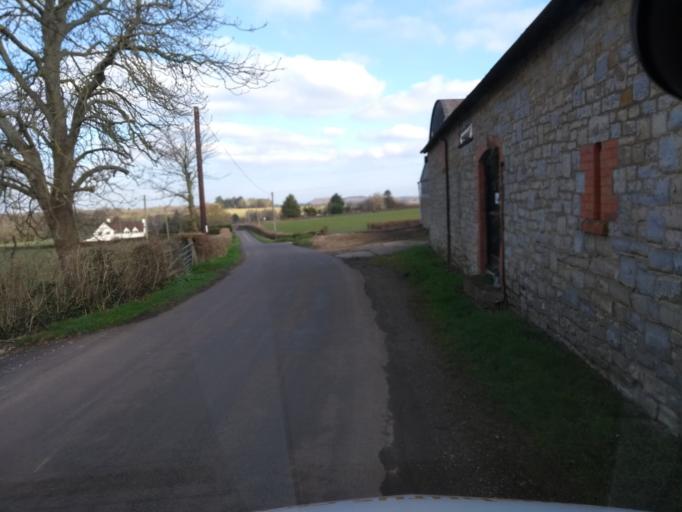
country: GB
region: England
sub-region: Somerset
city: Creech Saint Michael
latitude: 50.9564
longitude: -3.0274
